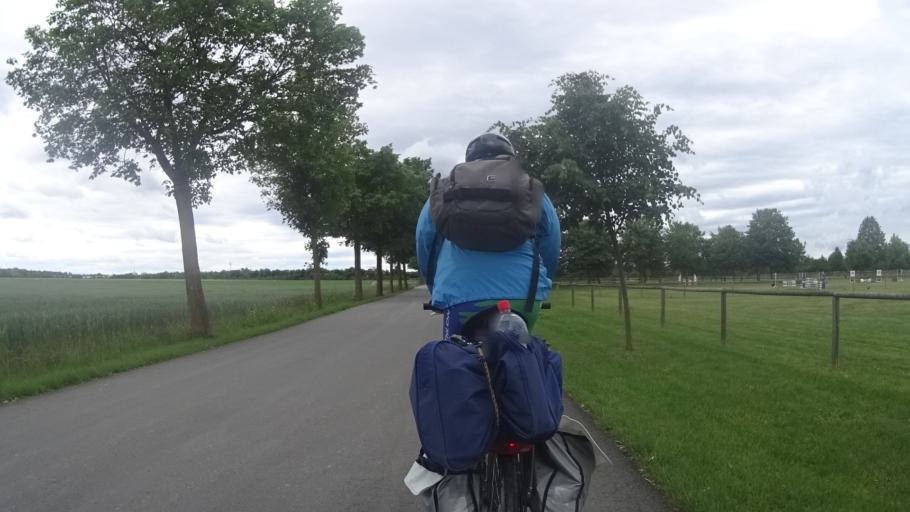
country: DE
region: Bavaria
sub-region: Upper Bavaria
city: Unterschleissheim
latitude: 48.2888
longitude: 11.5947
